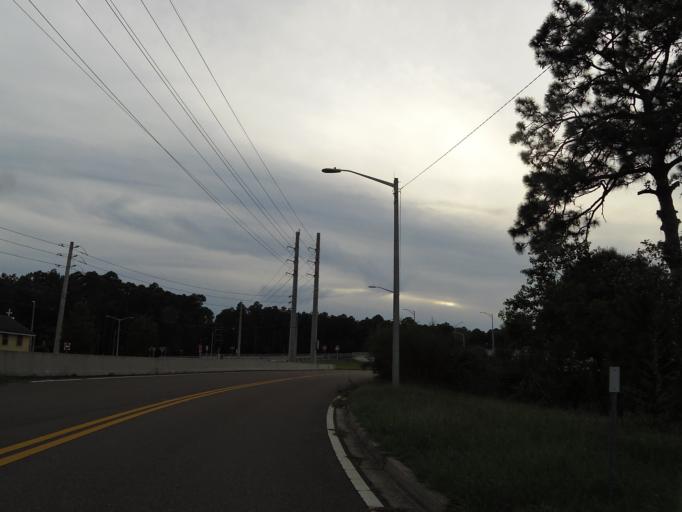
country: US
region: Florida
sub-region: Duval County
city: Jacksonville
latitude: 30.3597
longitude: -81.7116
